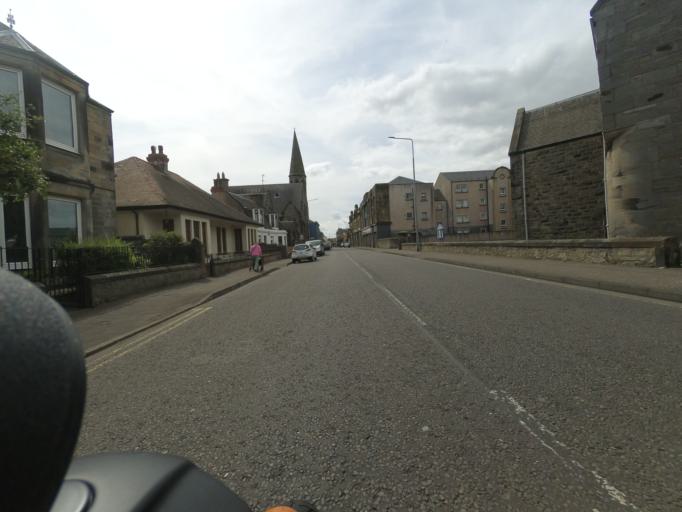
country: GB
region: Scotland
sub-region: Fife
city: Leven
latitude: 56.1973
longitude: -2.9952
